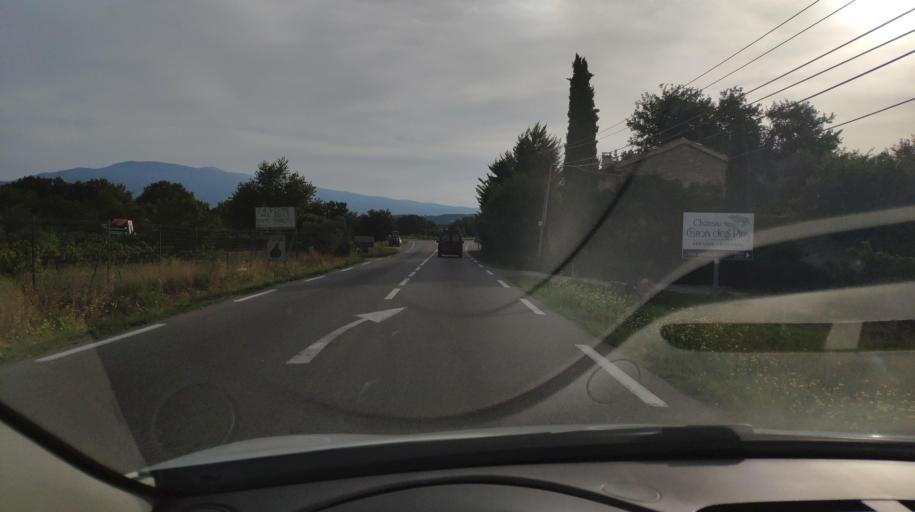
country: FR
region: Provence-Alpes-Cote d'Azur
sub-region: Departement du Vaucluse
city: Caromb
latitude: 44.0836
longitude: 5.1138
